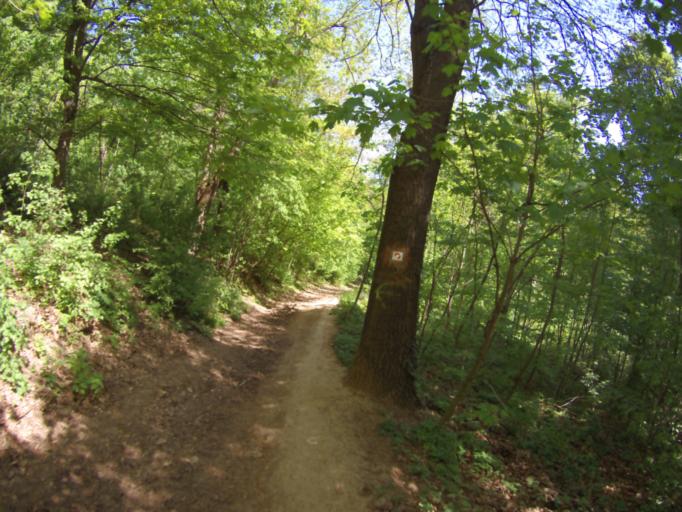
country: HU
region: Pest
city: Budaors
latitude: 47.4846
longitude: 18.9630
